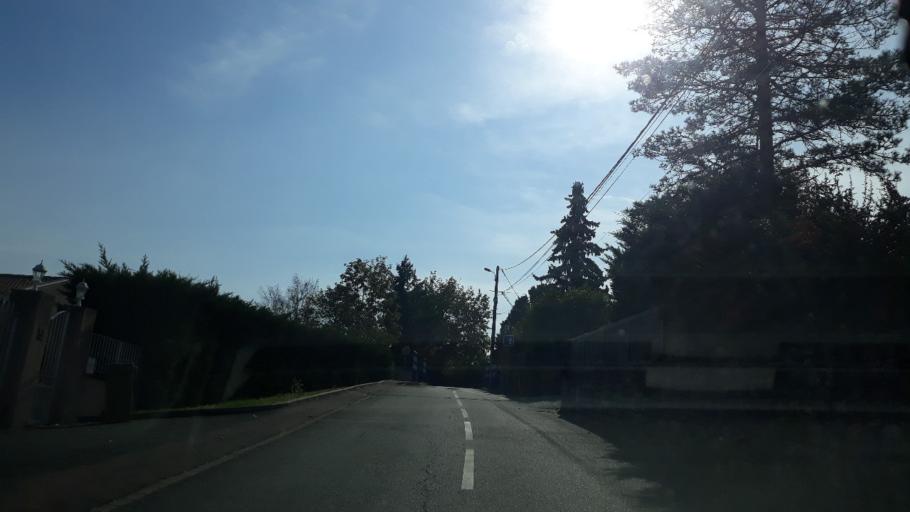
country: FR
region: Rhone-Alpes
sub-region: Departement du Rhone
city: Limas
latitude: 45.9717
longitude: 4.7082
